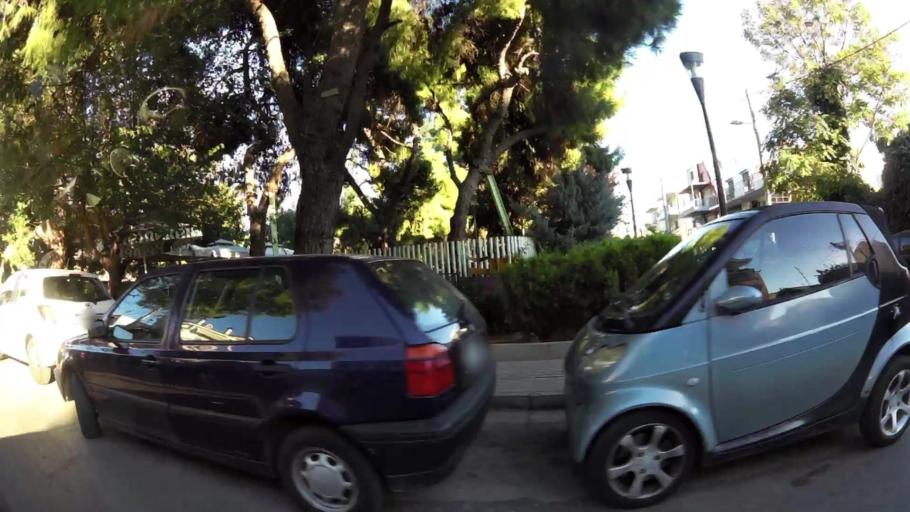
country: GR
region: Attica
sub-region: Nomarchia Athinas
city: Marousi
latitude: 38.0536
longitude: 23.8099
